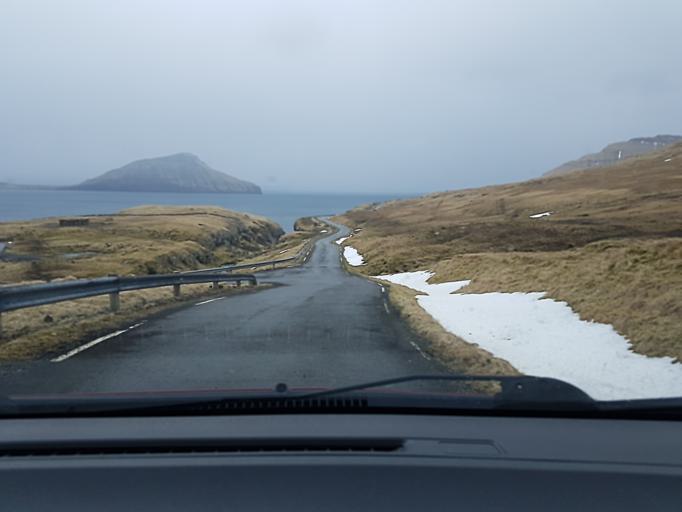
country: FO
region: Streymoy
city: Kollafjordhur
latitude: 62.0448
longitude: -6.9263
